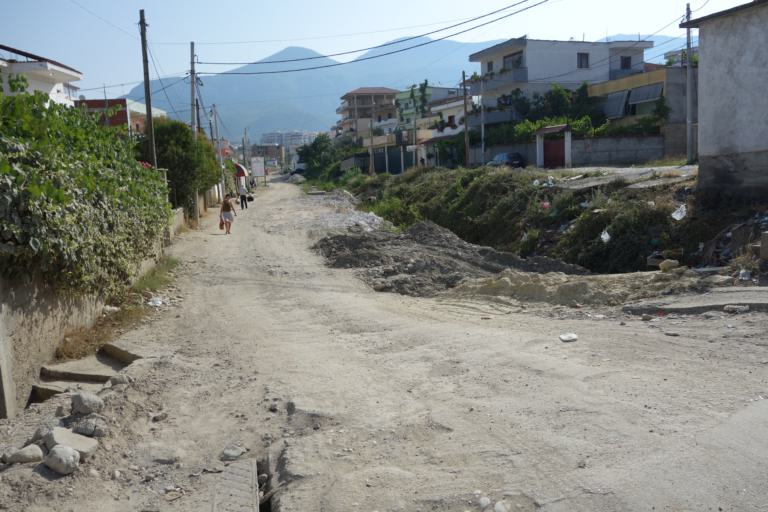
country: AL
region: Tirane
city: Tirana
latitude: 41.3401
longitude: 19.8480
